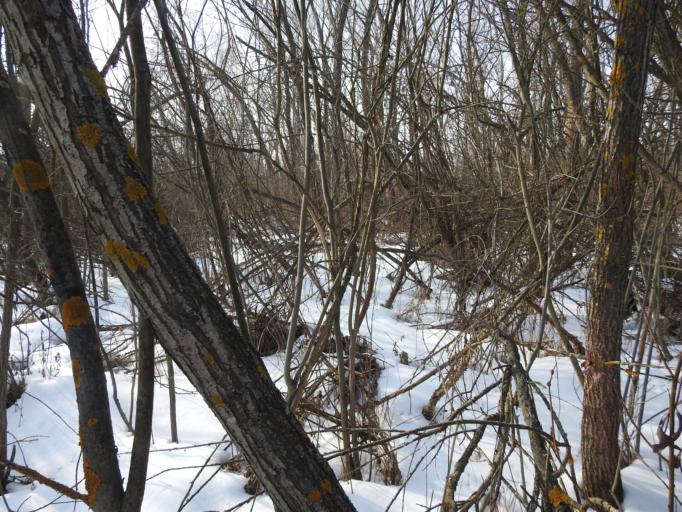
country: RU
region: Saratov
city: Sokolovyy
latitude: 51.5114
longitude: 45.7877
